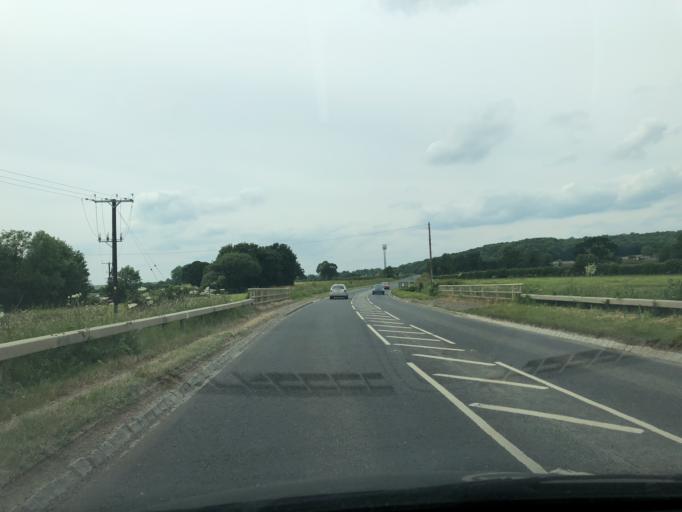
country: GB
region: England
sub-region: North Yorkshire
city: Great Habton
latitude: 54.2577
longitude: -0.8587
